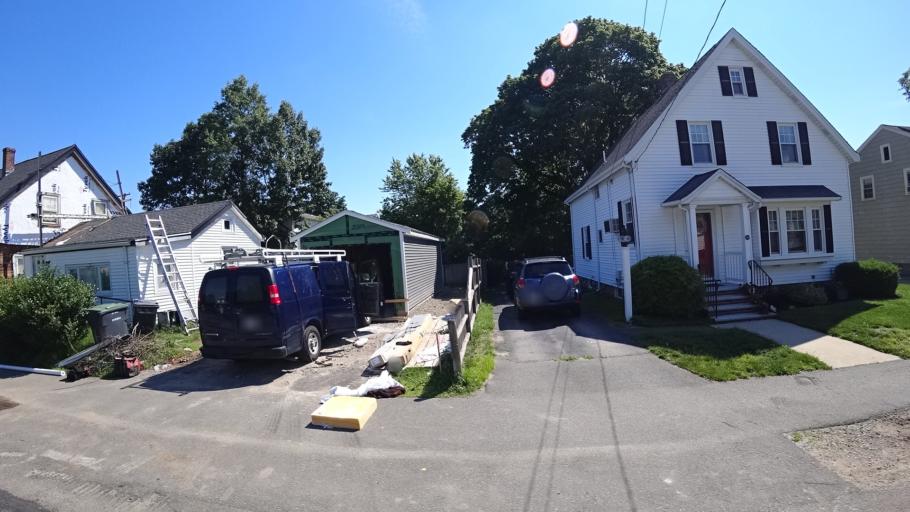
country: US
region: Massachusetts
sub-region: Norfolk County
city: Dedham
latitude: 42.2388
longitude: -71.1599
